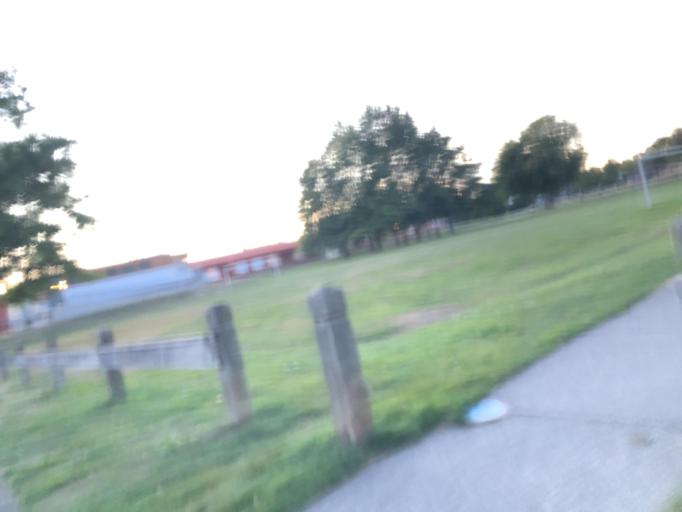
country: CA
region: British Columbia
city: Richmond
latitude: 49.1499
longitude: -123.1171
